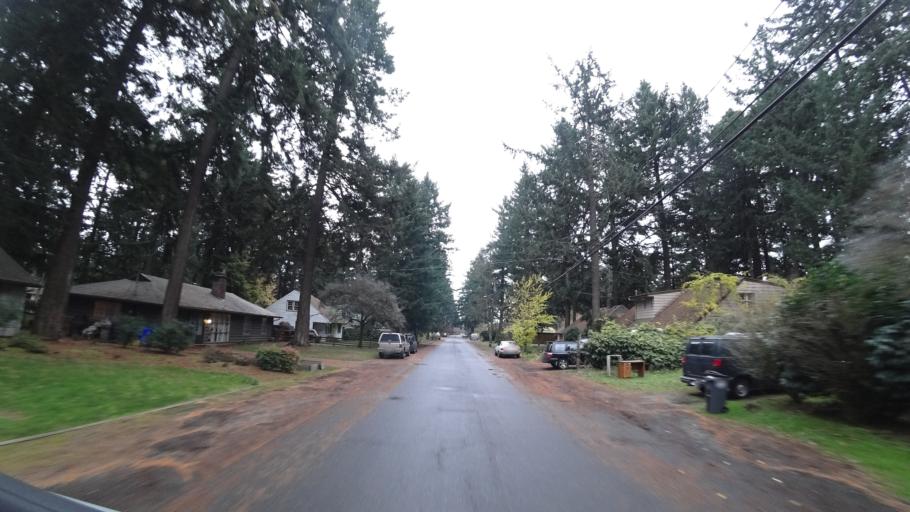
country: US
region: Oregon
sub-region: Multnomah County
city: Lents
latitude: 45.5307
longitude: -122.5472
